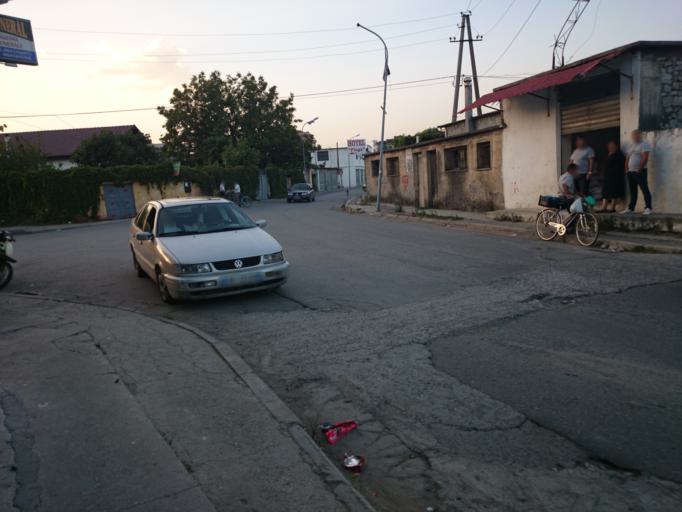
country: AL
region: Shkoder
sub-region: Rrethi i Shkodres
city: Shkoder
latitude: 42.0600
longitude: 19.5220
